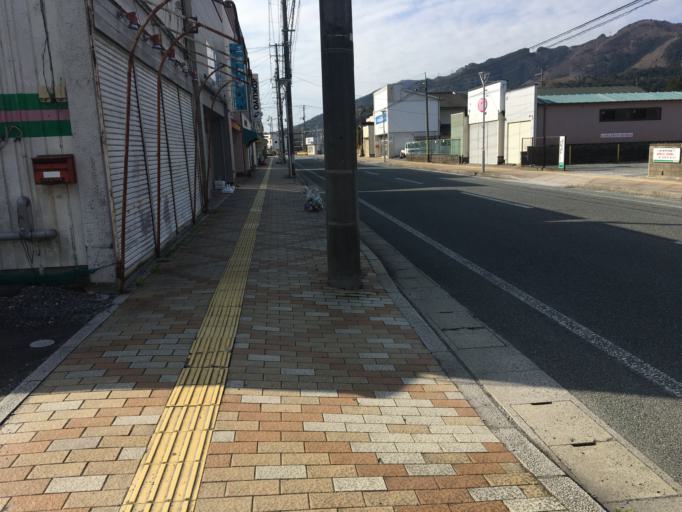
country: JP
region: Iwate
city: Ofunato
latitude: 39.0871
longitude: 141.7100
